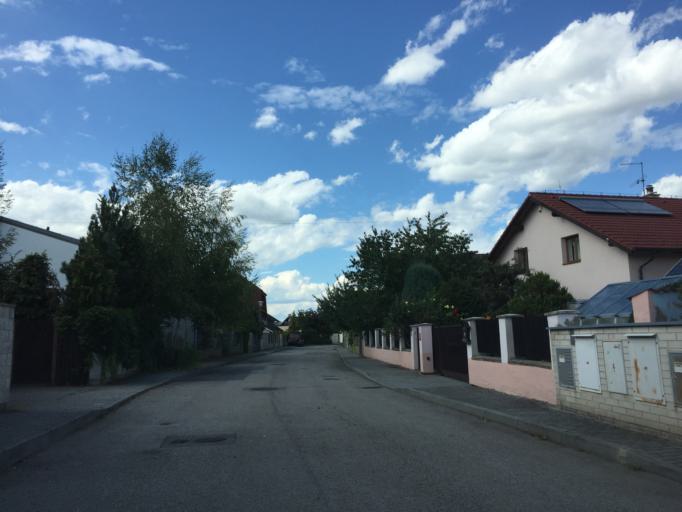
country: CZ
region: Jihocesky
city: Vcelna
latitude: 48.9421
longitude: 14.4777
